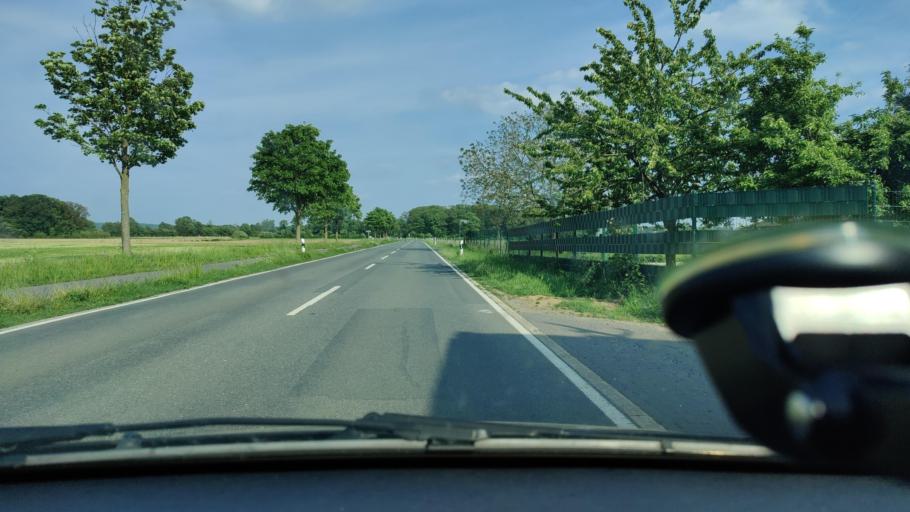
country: DE
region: North Rhine-Westphalia
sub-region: Regierungsbezirk Dusseldorf
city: Uedem
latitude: 51.6294
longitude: 6.2934
